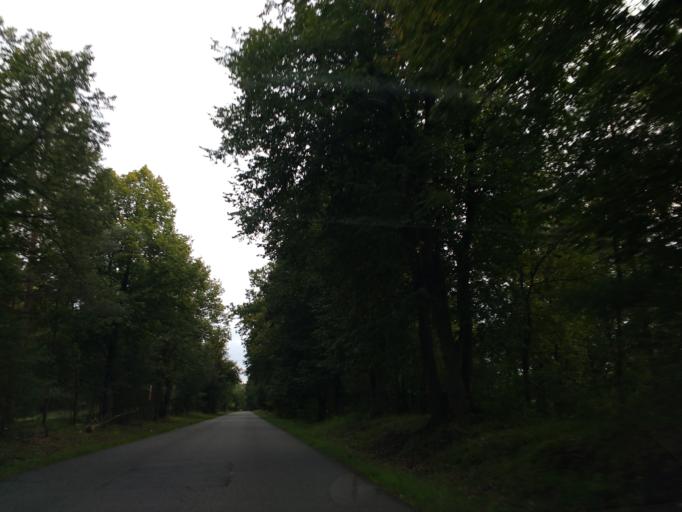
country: DE
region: North Rhine-Westphalia
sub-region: Regierungsbezirk Detmold
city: Hovelhof
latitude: 51.8037
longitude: 8.7223
